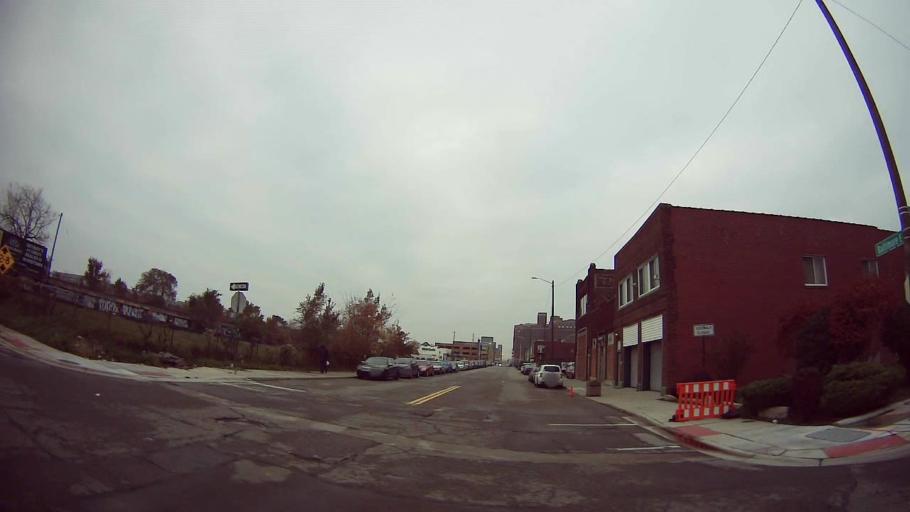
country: US
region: Michigan
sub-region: Wayne County
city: Hamtramck
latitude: 42.3693
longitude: -83.0699
